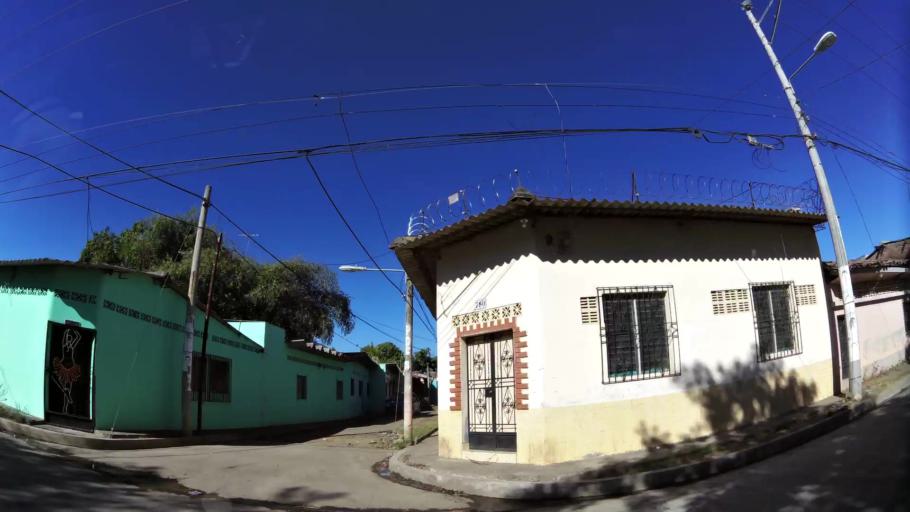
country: SV
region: San Miguel
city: San Miguel
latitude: 13.4669
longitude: -88.1726
